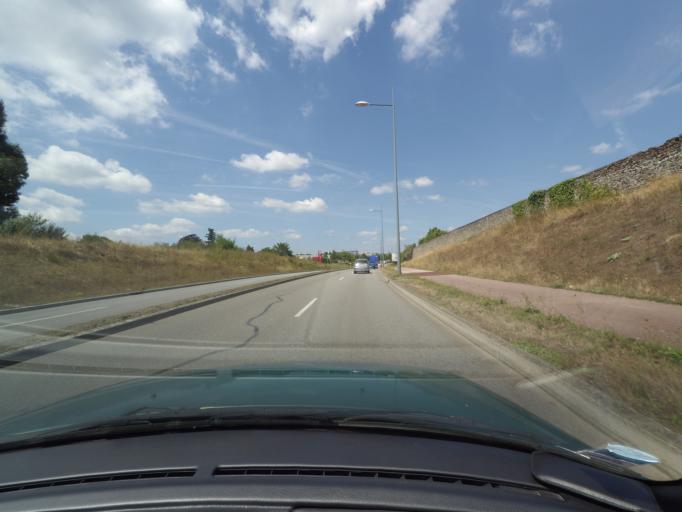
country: FR
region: Limousin
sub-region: Departement de la Haute-Vienne
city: Limoges
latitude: 45.8090
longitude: 1.2596
